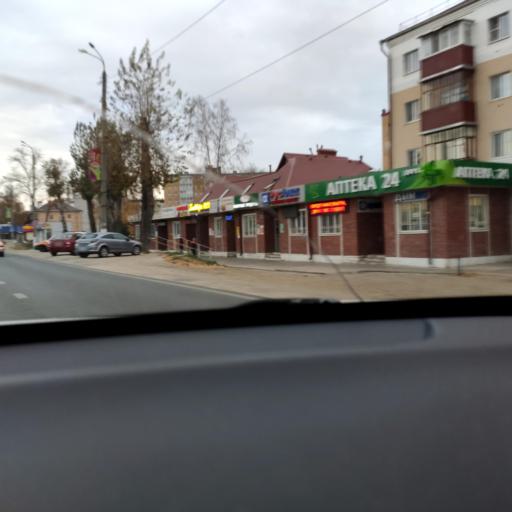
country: RU
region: Tatarstan
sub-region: Zelenodol'skiy Rayon
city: Zelenodolsk
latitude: 55.8481
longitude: 48.5599
